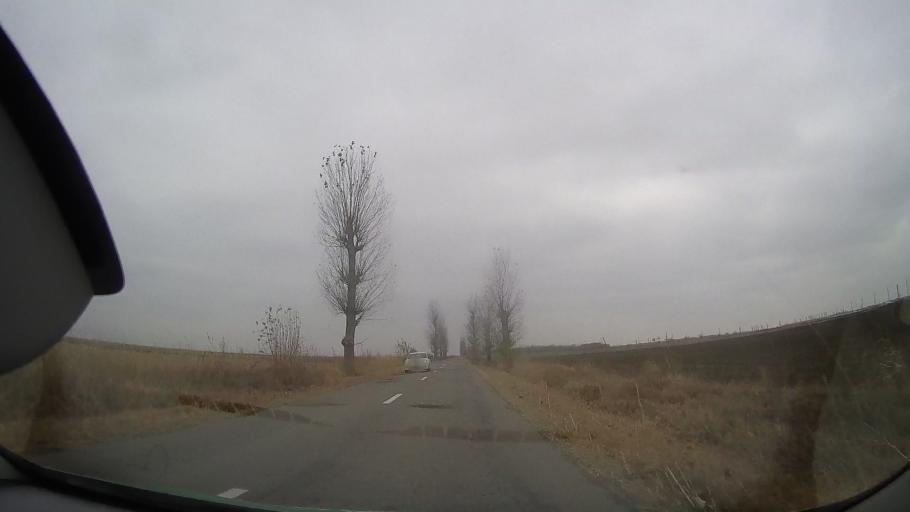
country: RO
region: Ialomita
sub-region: Comuna Valea Macrisului
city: Valea Macrisului
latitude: 44.7454
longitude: 26.8671
